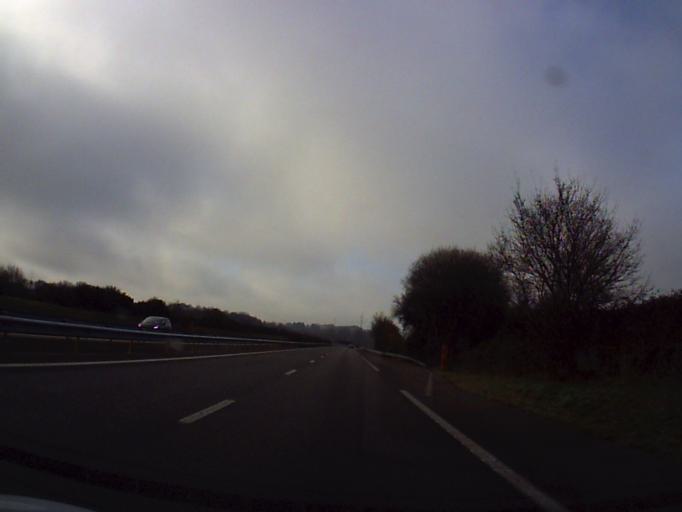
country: FR
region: Brittany
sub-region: Departement du Morbihan
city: Elven
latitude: 47.7322
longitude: -2.5817
